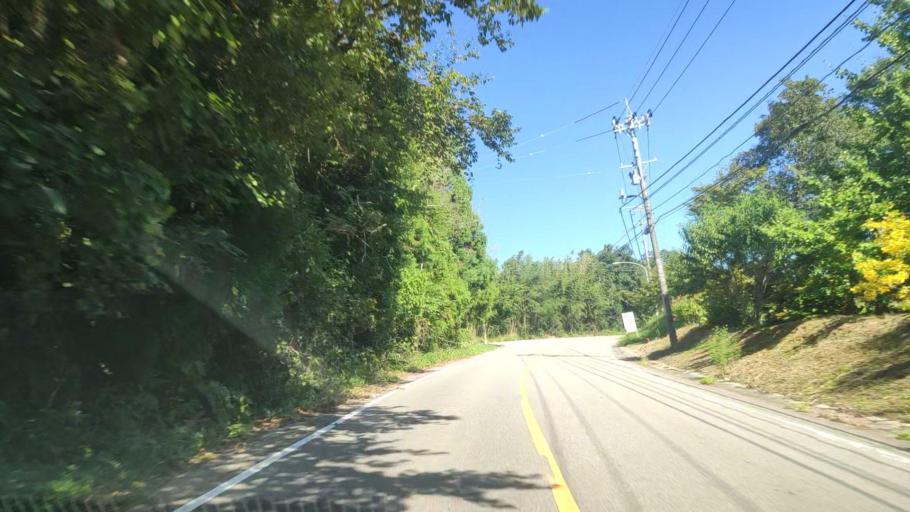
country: JP
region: Ishikawa
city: Nanao
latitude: 37.1696
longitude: 136.7142
